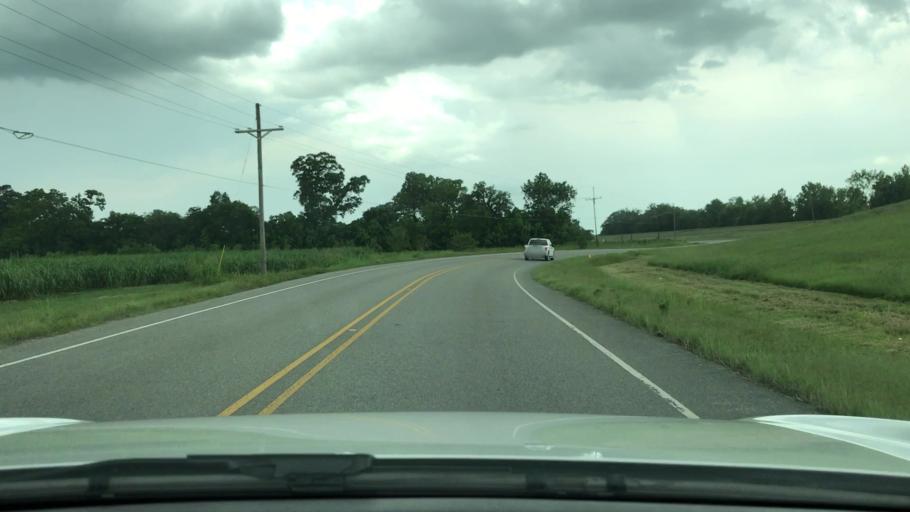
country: US
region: Louisiana
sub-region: Iberville Parish
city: Plaquemine
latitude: 30.2742
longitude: -91.2071
